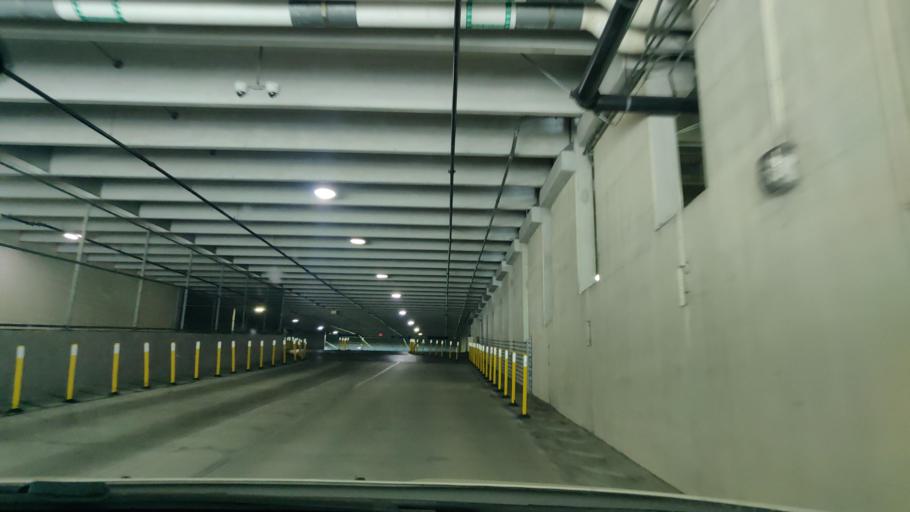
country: US
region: Florida
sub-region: Miami-Dade County
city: Sweetwater
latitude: 25.7602
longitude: -80.3740
